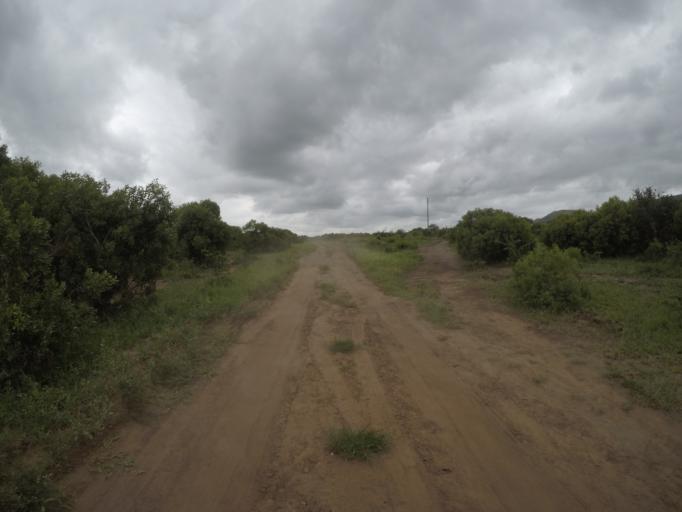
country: ZA
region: KwaZulu-Natal
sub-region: uThungulu District Municipality
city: Empangeni
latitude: -28.5837
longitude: 31.8616
